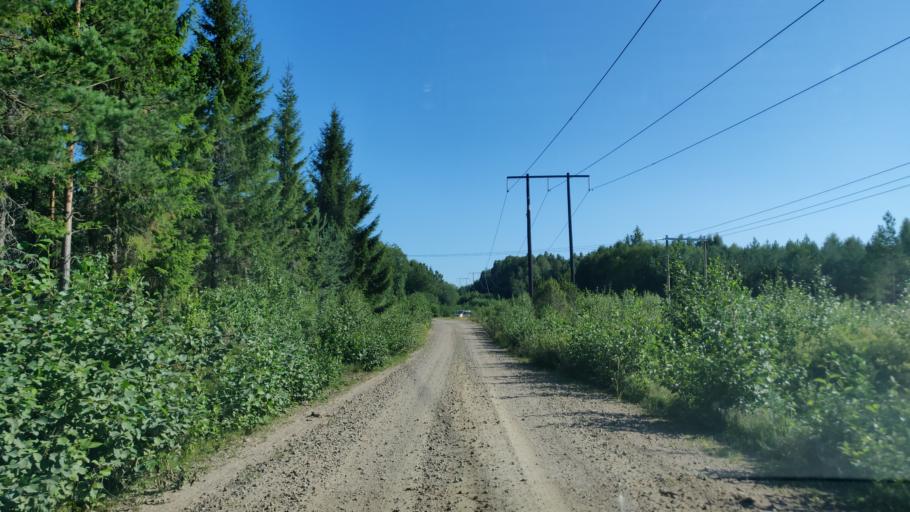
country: SE
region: Vaermland
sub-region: Hagfors Kommun
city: Ekshaerad
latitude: 60.0500
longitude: 13.5228
